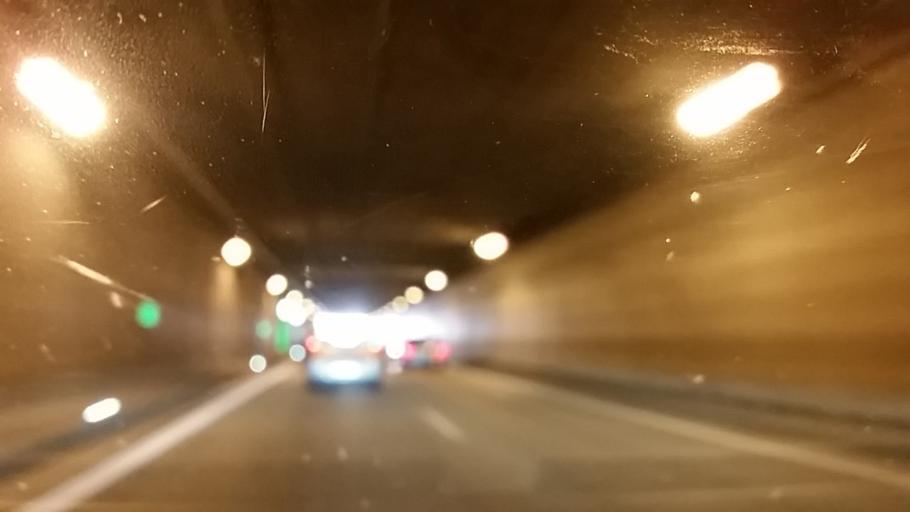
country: DE
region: North Rhine-Westphalia
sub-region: Regierungsbezirk Dusseldorf
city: Dusseldorf
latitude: 51.2294
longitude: 6.7412
